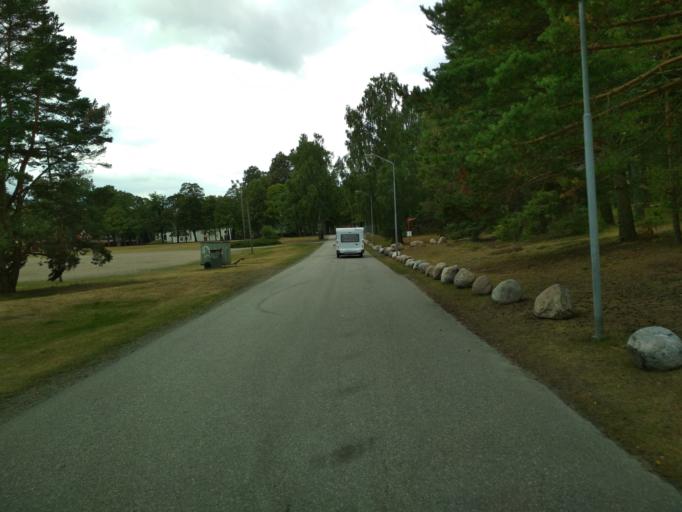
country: SE
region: Soedermanland
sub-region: Flens Kommun
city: Malmkoping
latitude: 59.1368
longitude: 16.7296
